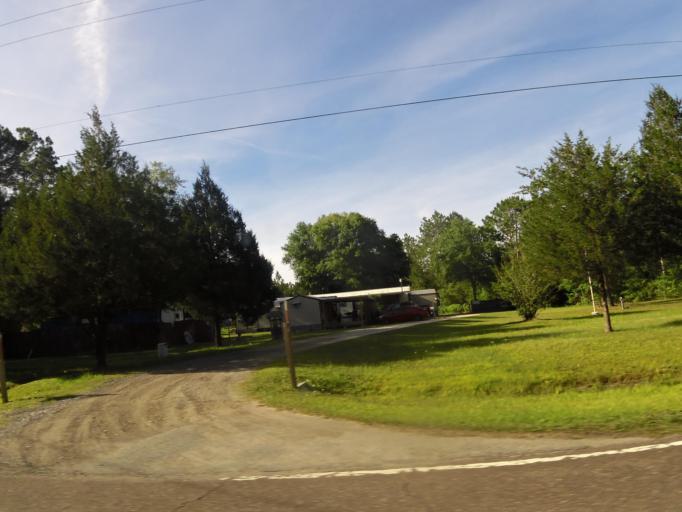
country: US
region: Florida
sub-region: Nassau County
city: Nassau Village-Ratliff
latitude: 30.4631
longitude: -81.7871
